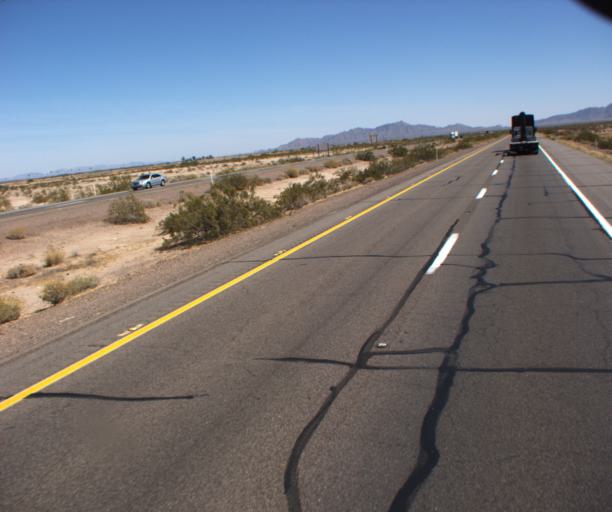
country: US
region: Arizona
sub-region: Yuma County
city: Wellton
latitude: 32.6967
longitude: -113.9314
